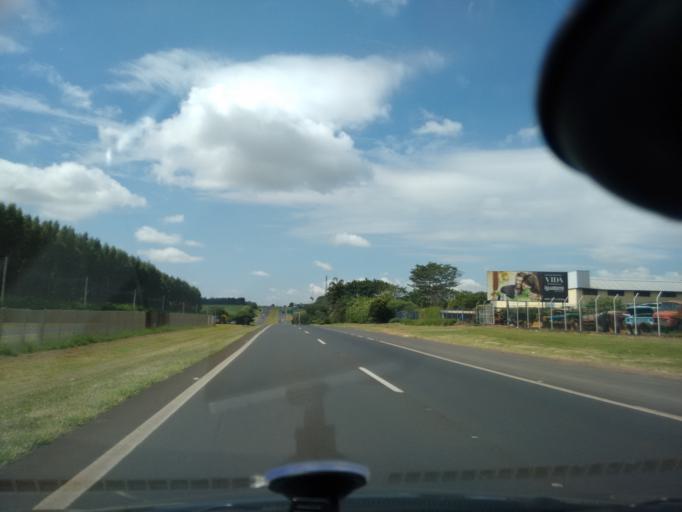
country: BR
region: Sao Paulo
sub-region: Ibate
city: Ibate
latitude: -21.9449
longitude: -48.0009
